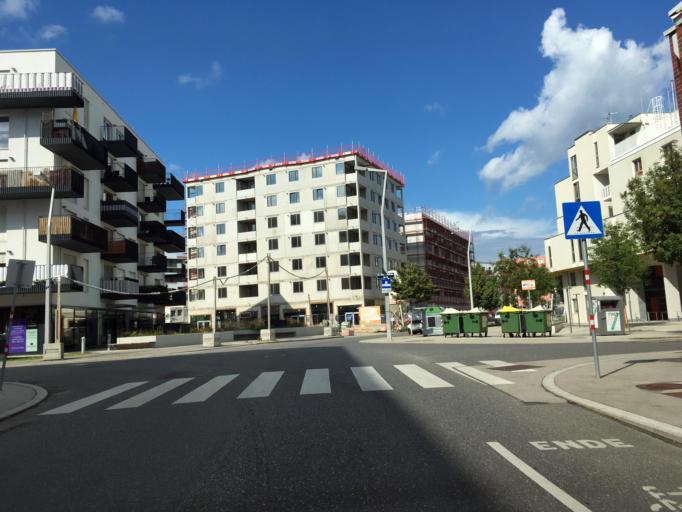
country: AT
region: Lower Austria
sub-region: Politischer Bezirk Wien-Umgebung
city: Gerasdorf bei Wien
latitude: 48.2297
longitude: 16.4593
